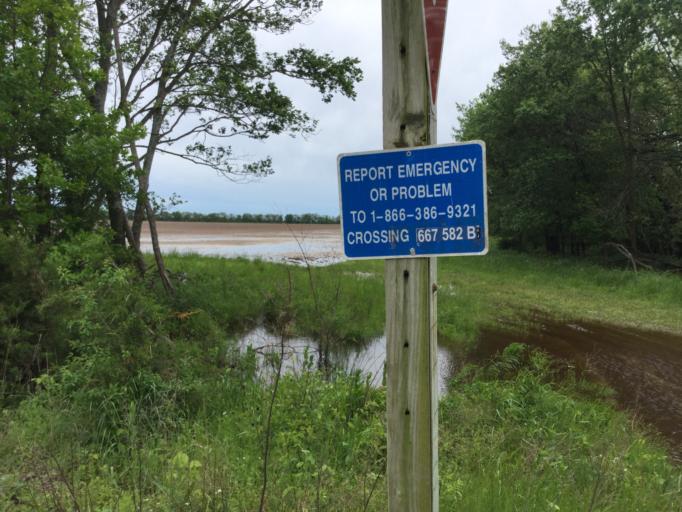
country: US
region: Kansas
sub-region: Labette County
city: Altamont
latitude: 37.1791
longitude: -95.2402
